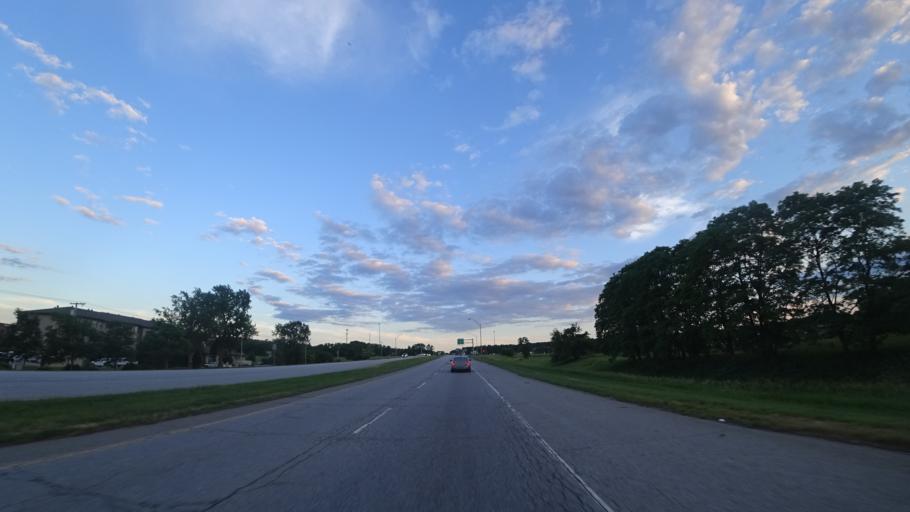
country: US
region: Indiana
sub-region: Porter County
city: Ogden Dunes
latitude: 41.6060
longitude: -87.1741
